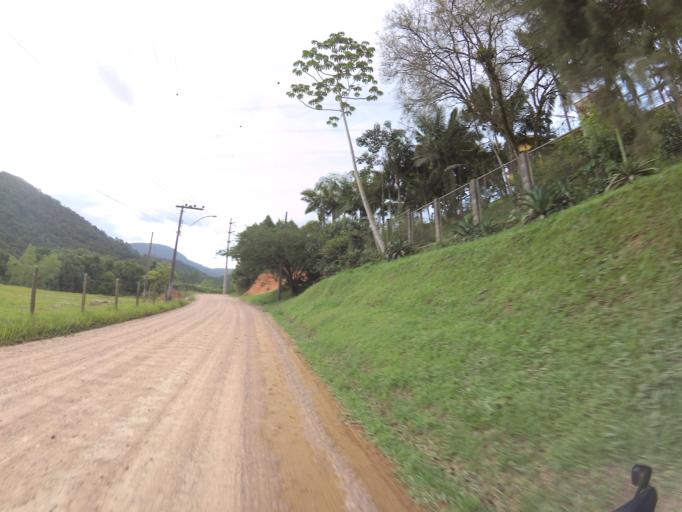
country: BR
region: Santa Catarina
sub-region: Pomerode
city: Pomerode
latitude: -26.7854
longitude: -49.1633
